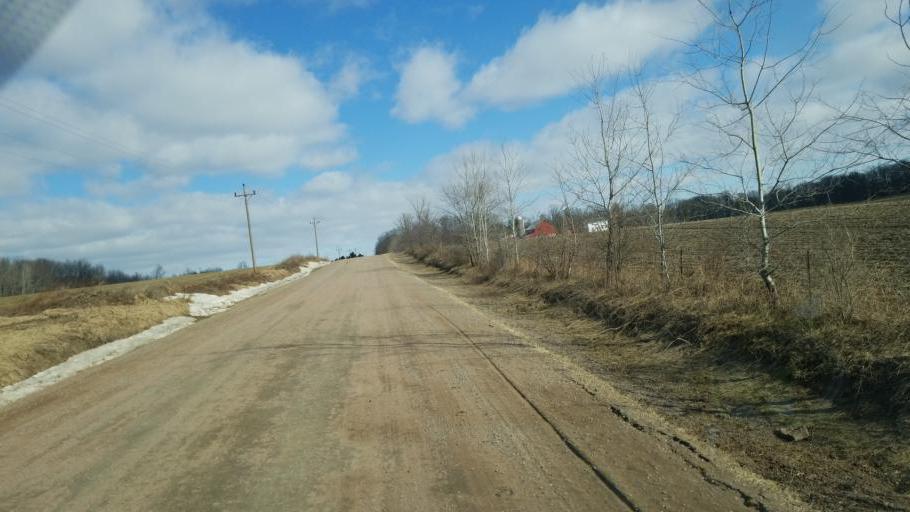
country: US
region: Wisconsin
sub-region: Clark County
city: Loyal
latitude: 44.6359
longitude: -90.4359
